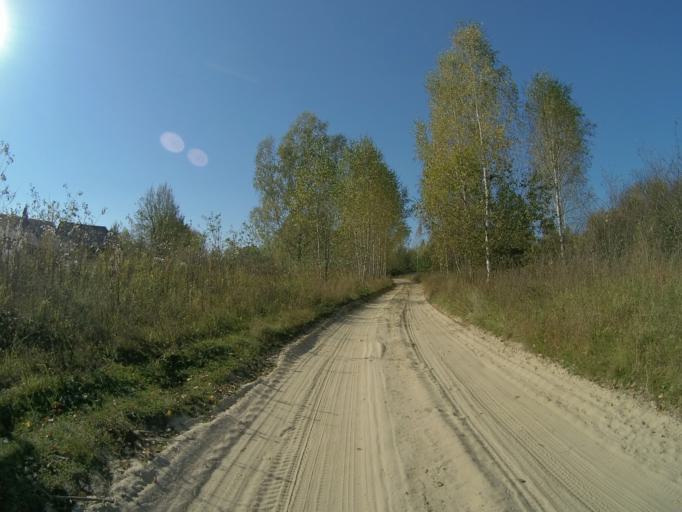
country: RU
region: Vladimir
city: Vorsha
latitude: 55.9741
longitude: 40.1689
